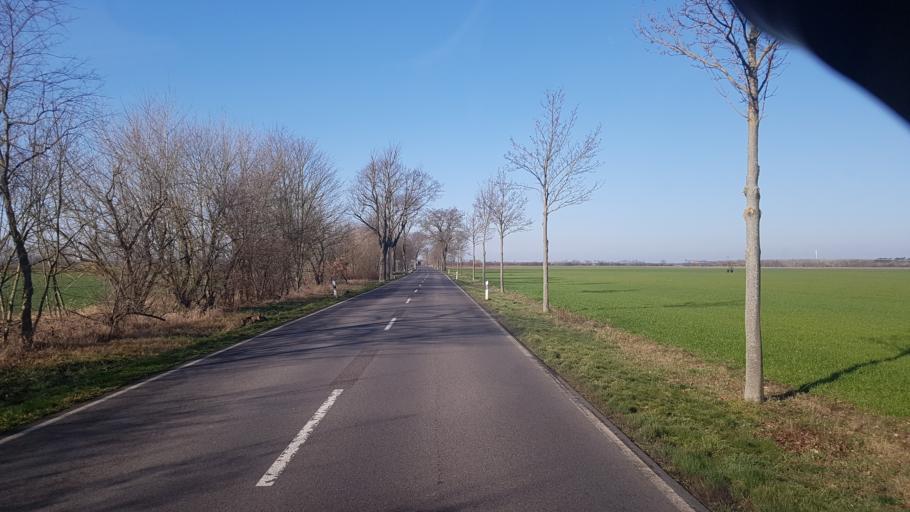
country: DE
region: Brandenburg
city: Luckau
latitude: 51.8499
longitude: 13.7871
